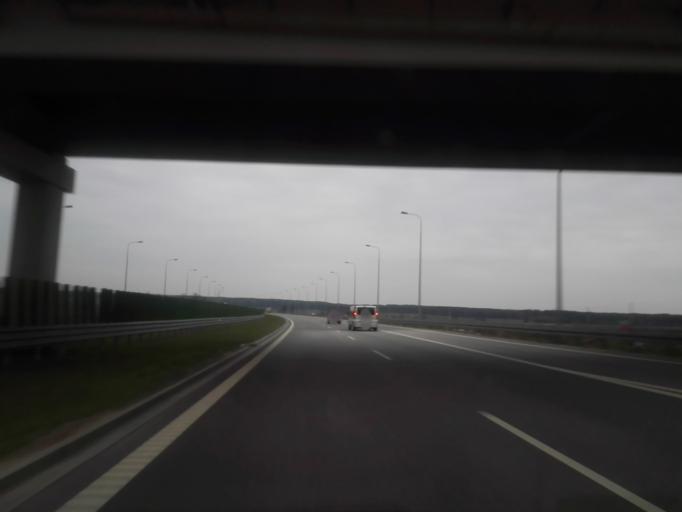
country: PL
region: Podlasie
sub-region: Powiat kolnenski
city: Stawiski
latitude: 53.3867
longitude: 22.1443
